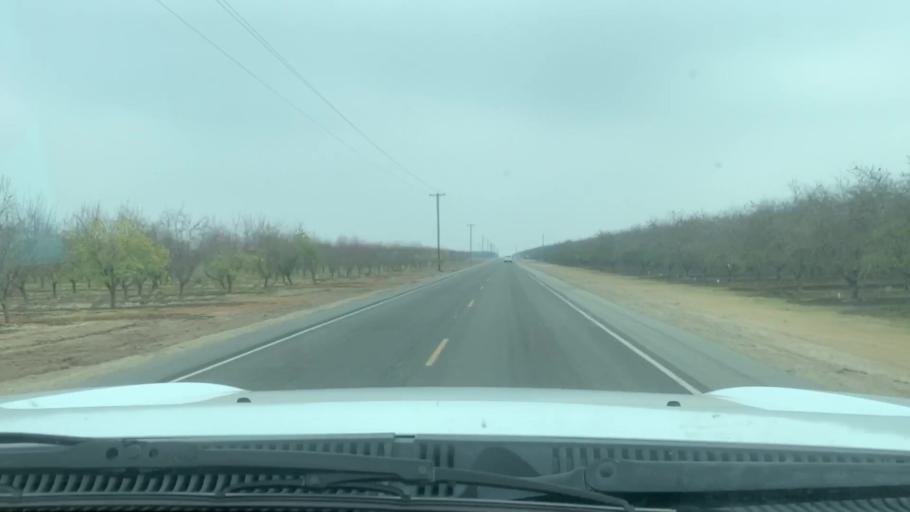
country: US
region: California
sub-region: Kern County
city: Buttonwillow
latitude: 35.5004
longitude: -119.4117
